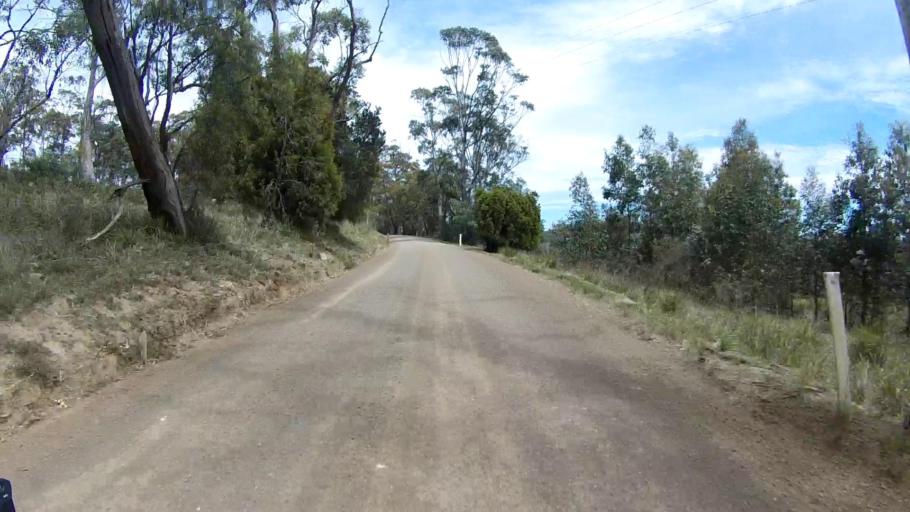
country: AU
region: Tasmania
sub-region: Sorell
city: Sorell
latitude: -42.7928
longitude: 147.6926
